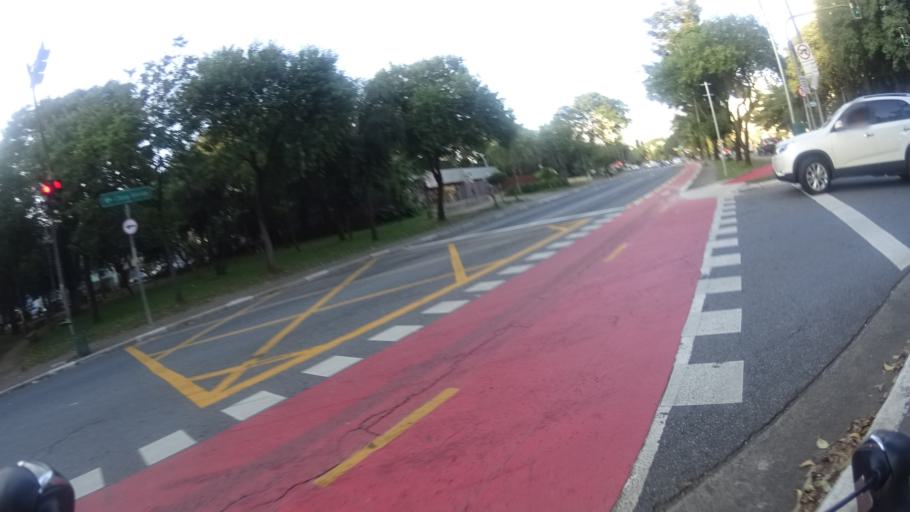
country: BR
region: Sao Paulo
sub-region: Sao Paulo
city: Sao Paulo
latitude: -23.4830
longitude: -46.6329
